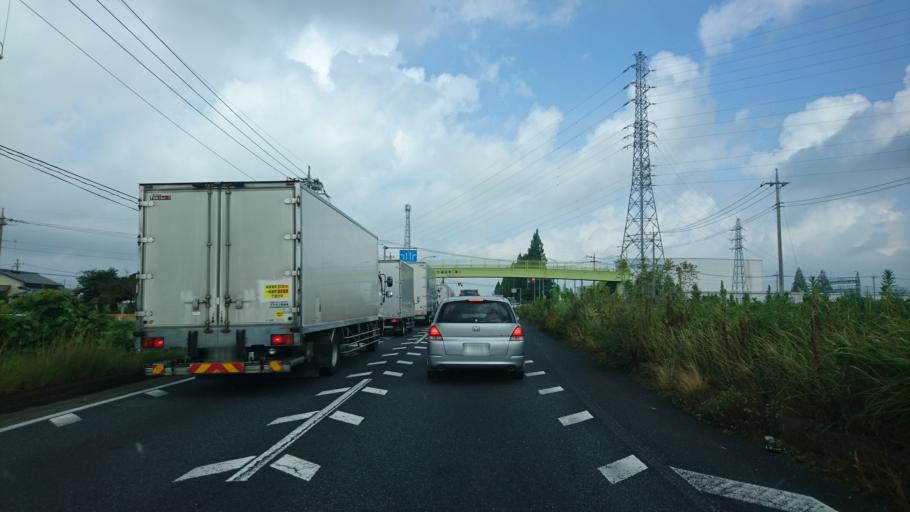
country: JP
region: Gunma
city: Tatebayashi
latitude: 36.2902
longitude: 139.4972
